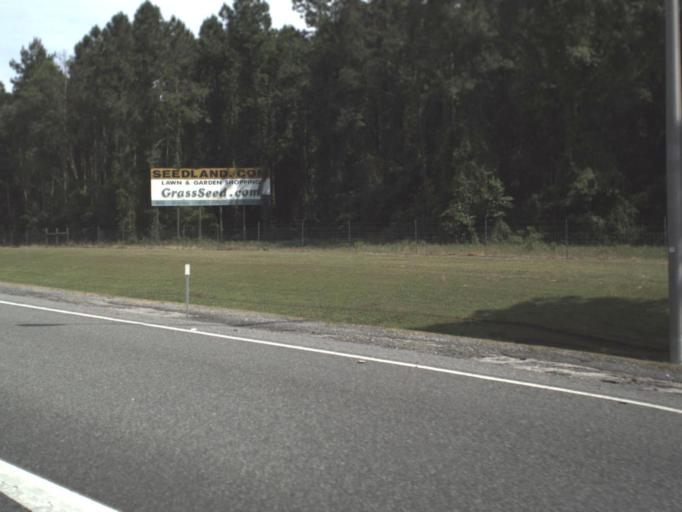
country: US
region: Florida
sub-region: Suwannee County
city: Wellborn
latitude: 30.2745
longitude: -82.7976
